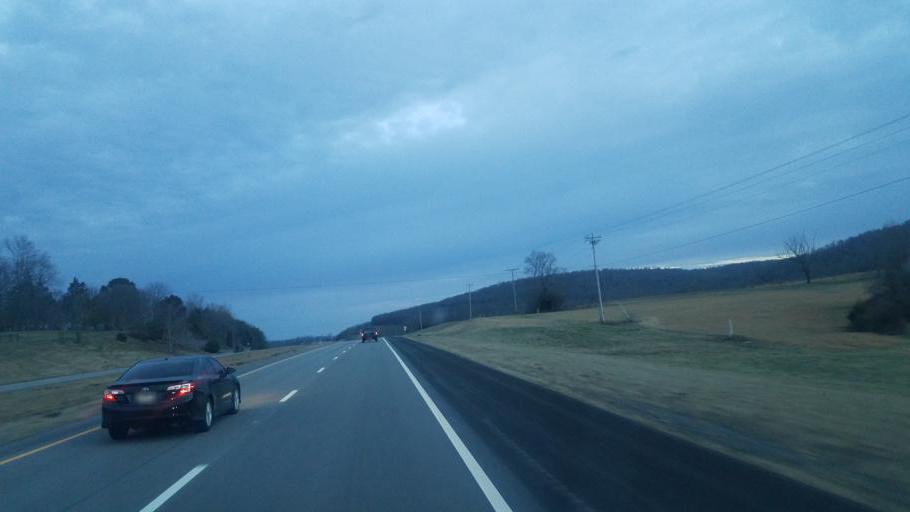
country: US
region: Tennessee
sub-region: White County
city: Sparta
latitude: 35.8378
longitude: -85.4640
